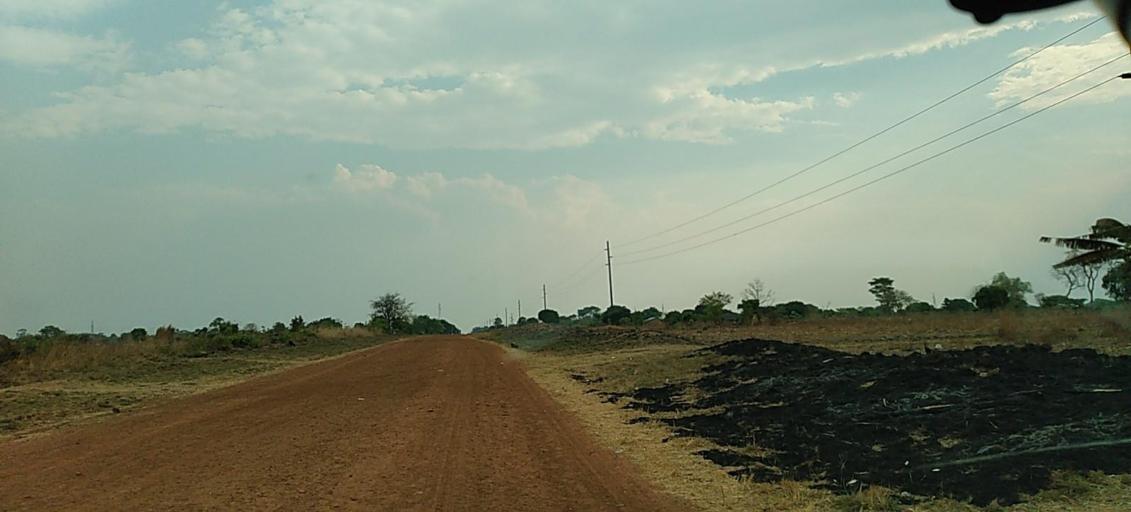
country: ZM
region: North-Western
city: Kabompo
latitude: -13.8688
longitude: 23.6688
